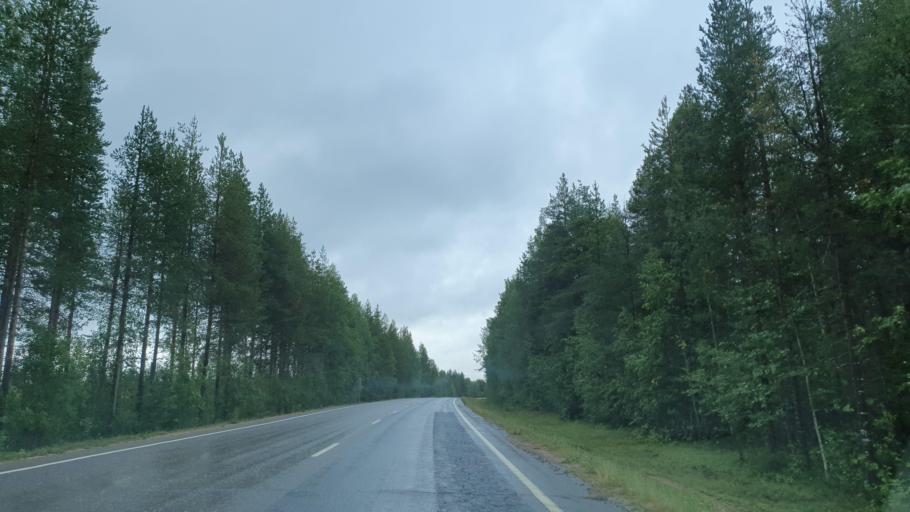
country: FI
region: Lapland
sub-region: Tunturi-Lappi
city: Kolari
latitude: 67.2775
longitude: 23.8643
